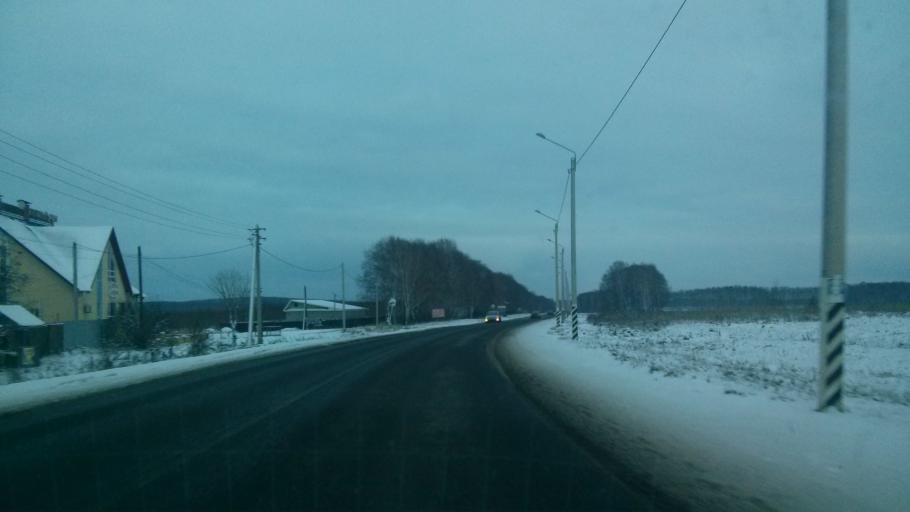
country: RU
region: Nizjnij Novgorod
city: Bogorodsk
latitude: 56.0646
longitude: 43.4252
